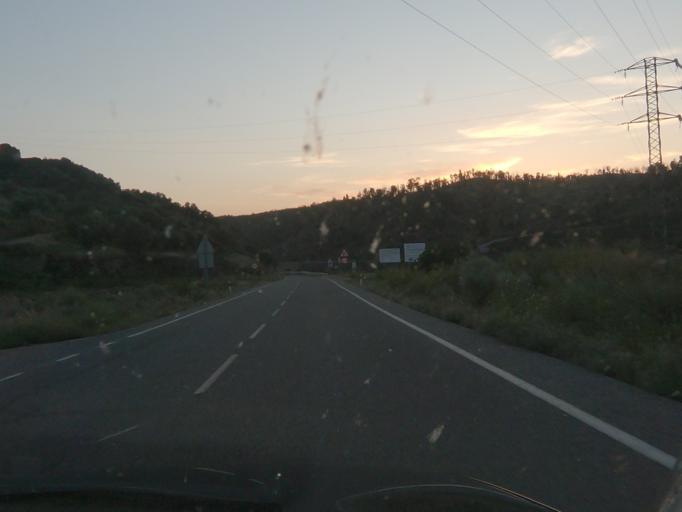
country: ES
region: Extremadura
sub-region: Provincia de Caceres
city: Alcantara
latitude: 39.7229
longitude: -6.8849
